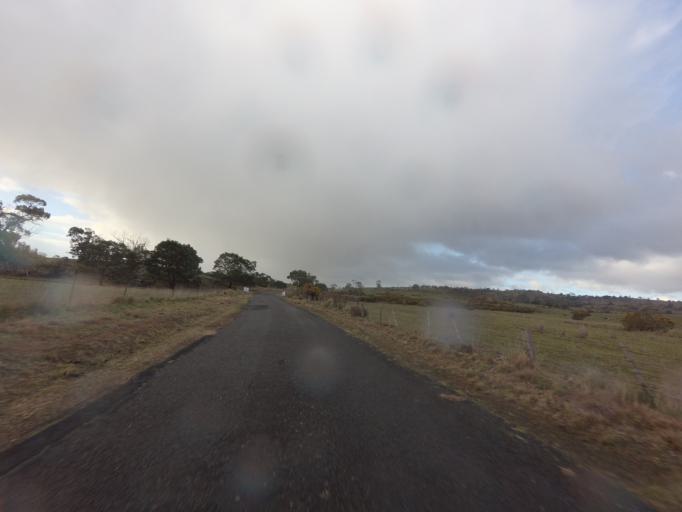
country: AU
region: Tasmania
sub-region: Break O'Day
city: St Helens
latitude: -42.0001
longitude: 148.0886
